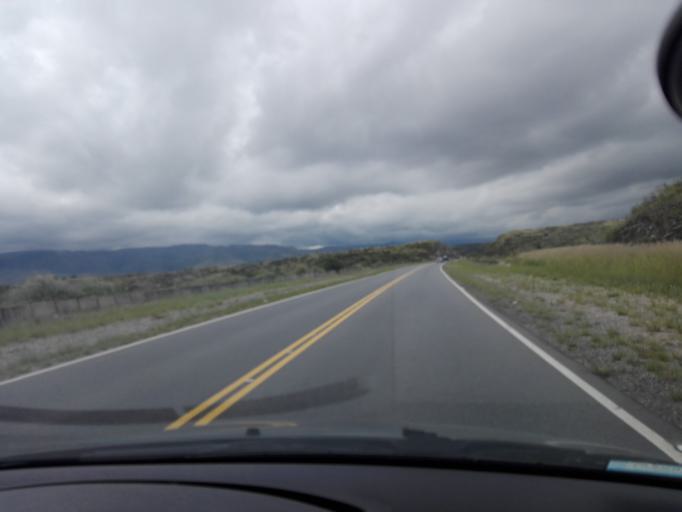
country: AR
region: Cordoba
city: Cuesta Blanca
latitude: -31.5815
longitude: -64.6346
